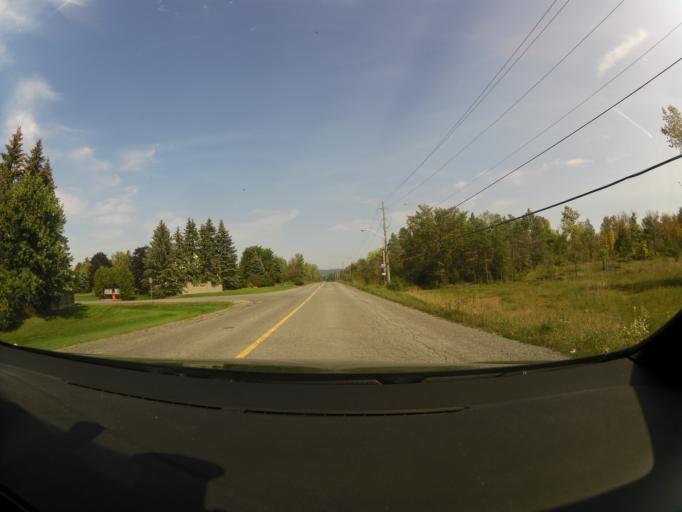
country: CA
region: Ontario
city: Bells Corners
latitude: 45.4430
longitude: -75.9857
